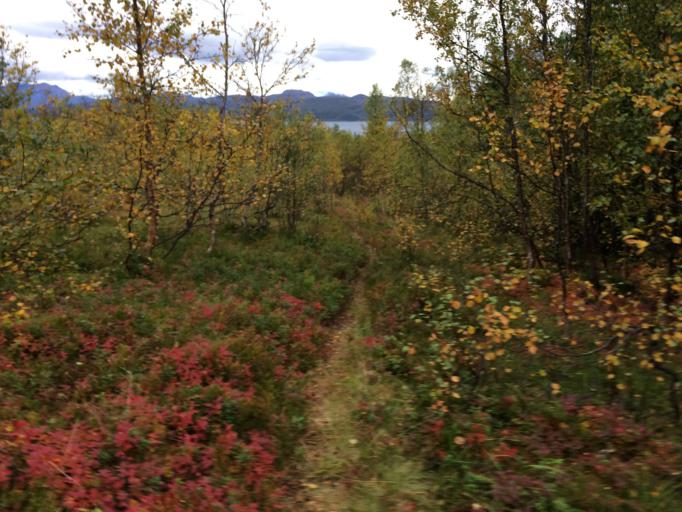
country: NO
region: Troms
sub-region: Sorreisa
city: Sorreisa
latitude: 69.5347
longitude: 18.3104
